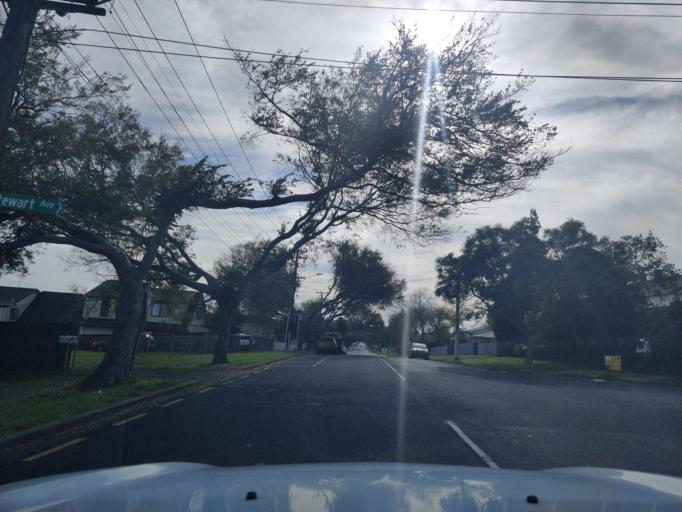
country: NZ
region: Auckland
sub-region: Auckland
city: Tamaki
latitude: -36.8962
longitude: 174.8548
